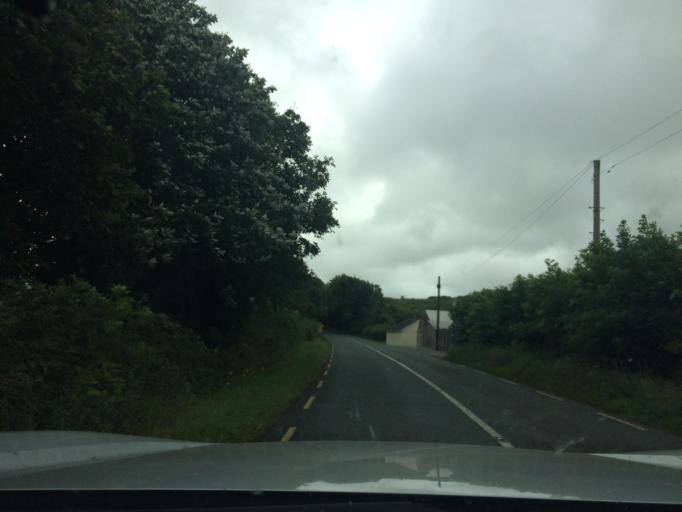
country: IE
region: Munster
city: Cashel
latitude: 52.4747
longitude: -7.8461
